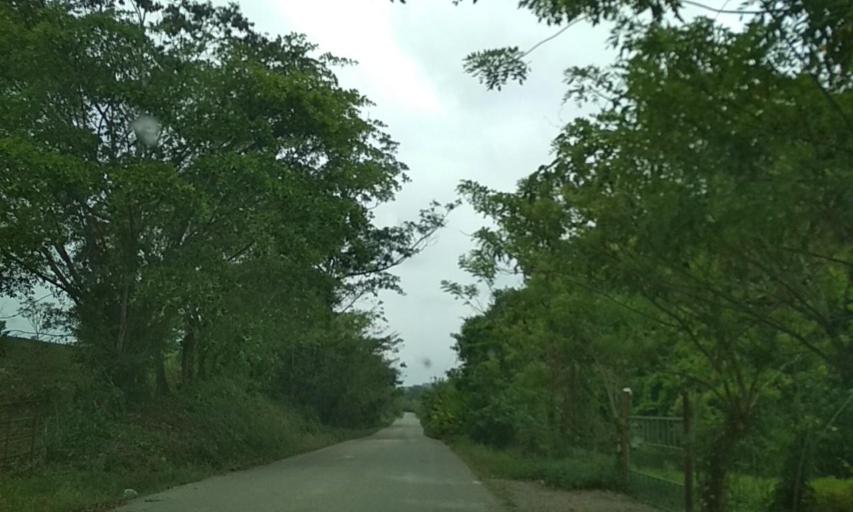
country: MX
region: Veracruz
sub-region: Uxpanapa
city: Poblado 10
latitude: 17.4681
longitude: -94.1133
